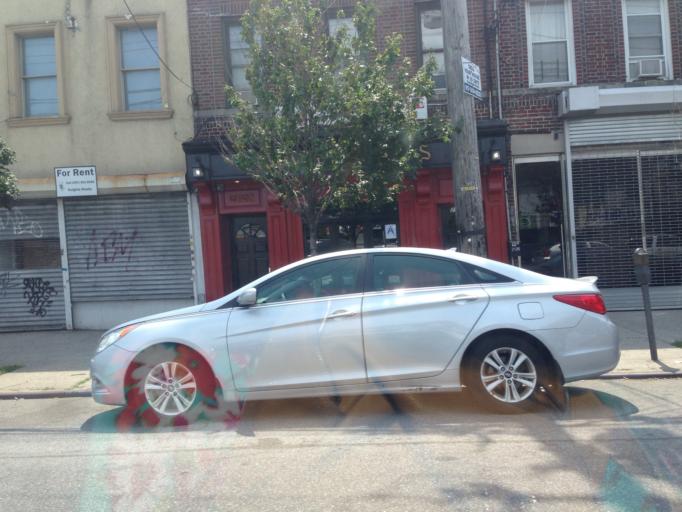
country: US
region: New York
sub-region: Kings County
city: Brooklyn
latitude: 40.6181
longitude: -73.9321
